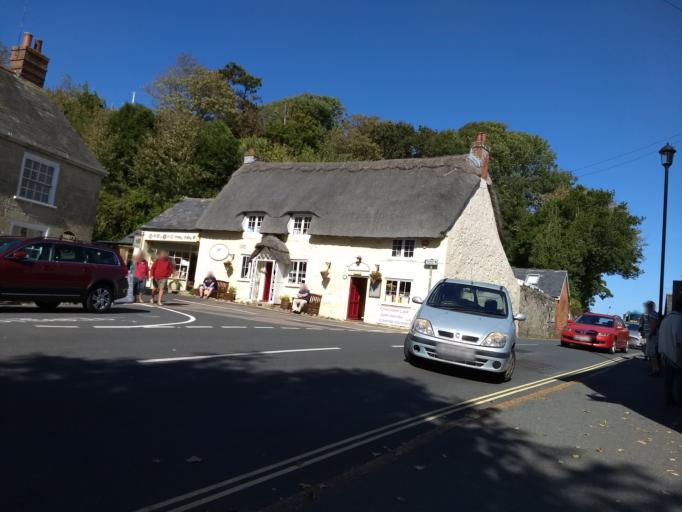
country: GB
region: England
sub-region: Isle of Wight
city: Niton
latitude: 50.6331
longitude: -1.2545
